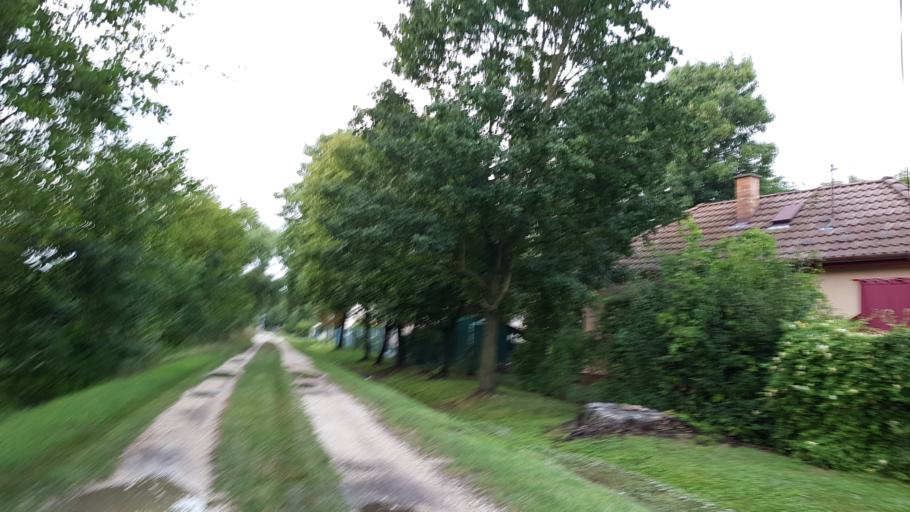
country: HU
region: Fejer
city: Gardony
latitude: 47.1924
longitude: 18.6040
